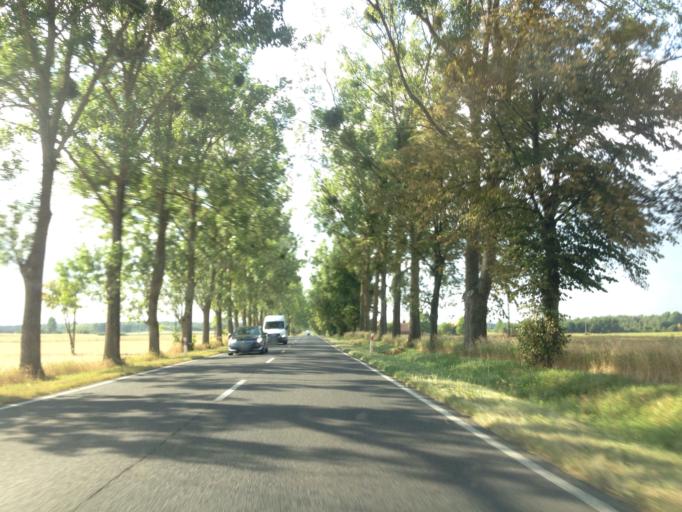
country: PL
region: Kujawsko-Pomorskie
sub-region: Powiat swiecki
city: Bukowiec
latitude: 53.4578
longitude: 18.1948
